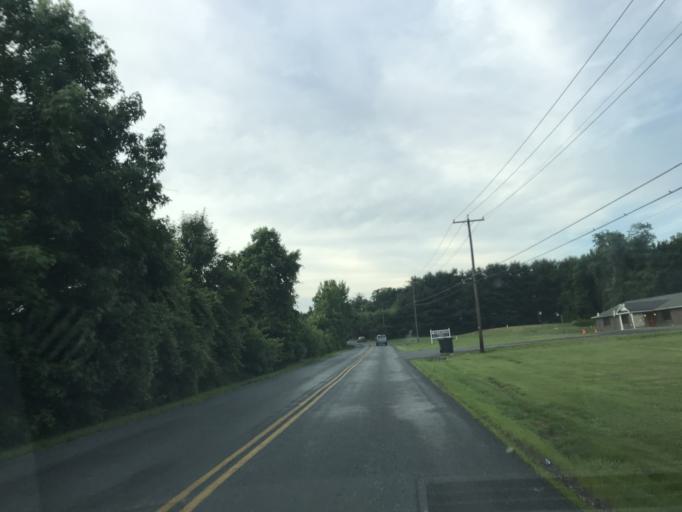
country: US
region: Maryland
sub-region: Harford County
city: Perryman
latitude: 39.5103
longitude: -76.2064
